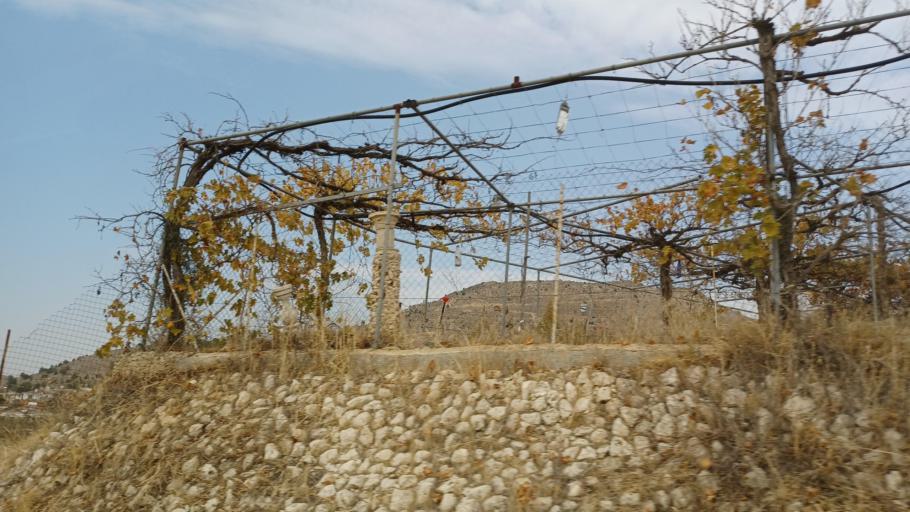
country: CY
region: Lefkosia
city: Klirou
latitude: 35.0381
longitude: 33.1326
